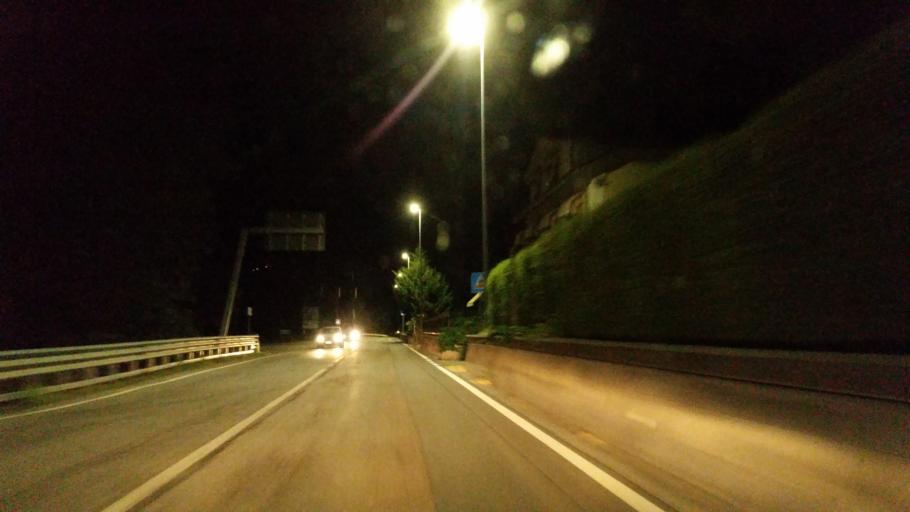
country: IT
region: Piedmont
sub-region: Provincia di Cuneo
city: Camerana
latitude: 44.4386
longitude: 8.1520
